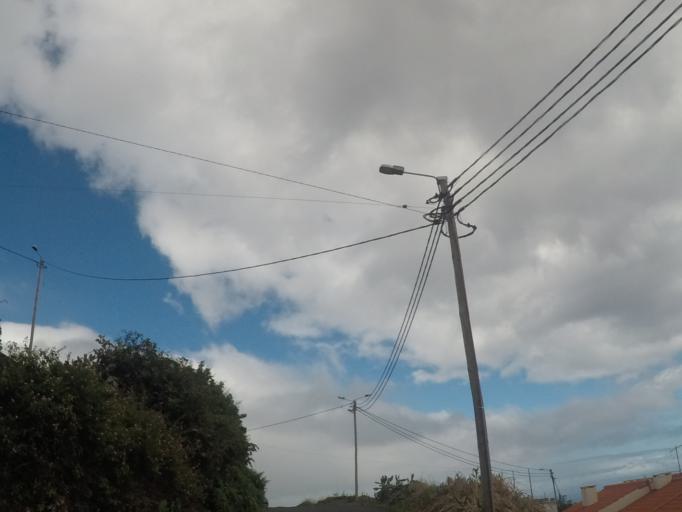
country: PT
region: Madeira
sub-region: Santa Cruz
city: Camacha
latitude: 32.6610
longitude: -16.8279
